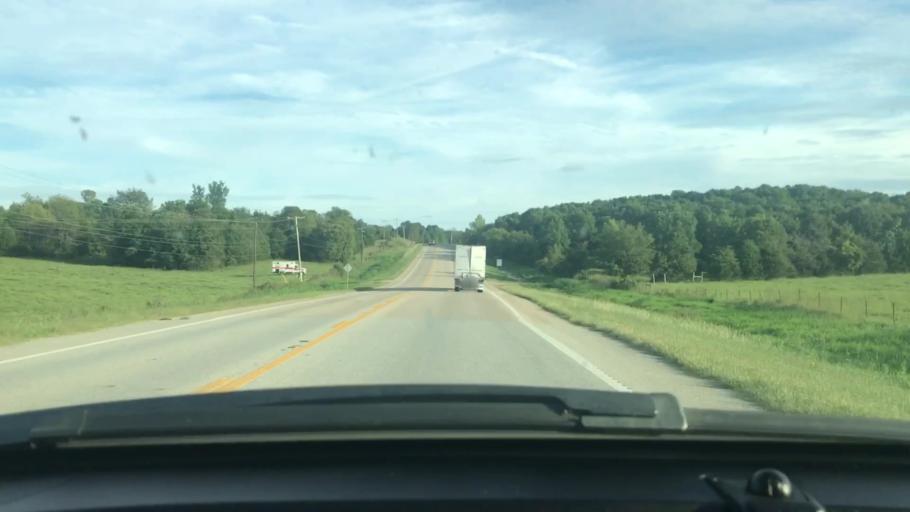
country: US
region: Arkansas
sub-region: Randolph County
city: Pocahontas
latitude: 36.1926
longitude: -91.1657
